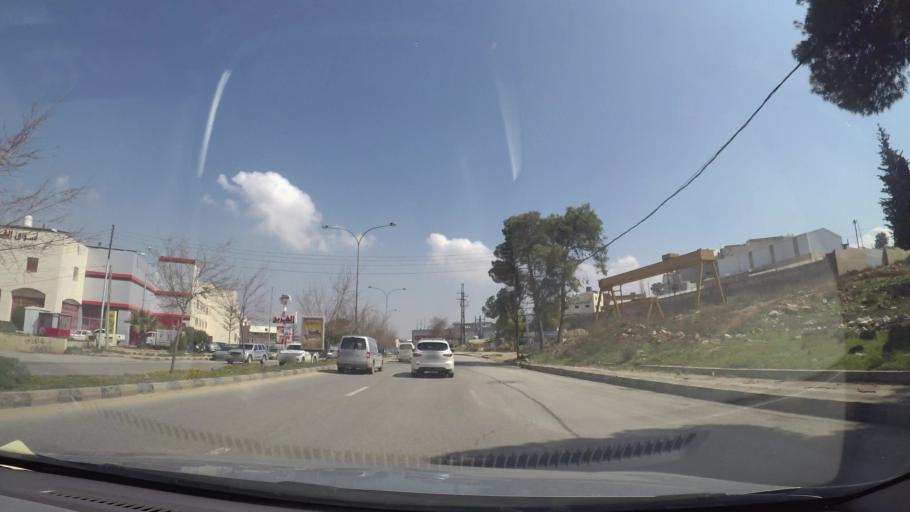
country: JO
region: Amman
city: Al Bunayyat ash Shamaliyah
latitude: 31.9130
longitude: 35.9006
